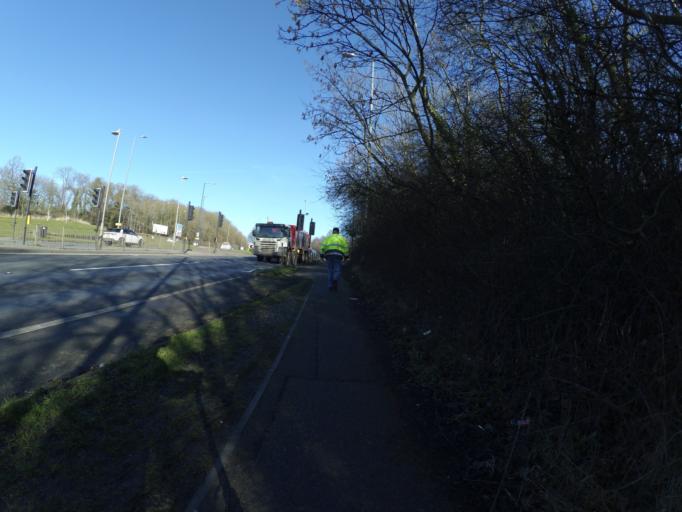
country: GB
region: England
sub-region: Warwickshire
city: Rugby
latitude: 52.3941
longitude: -1.2498
